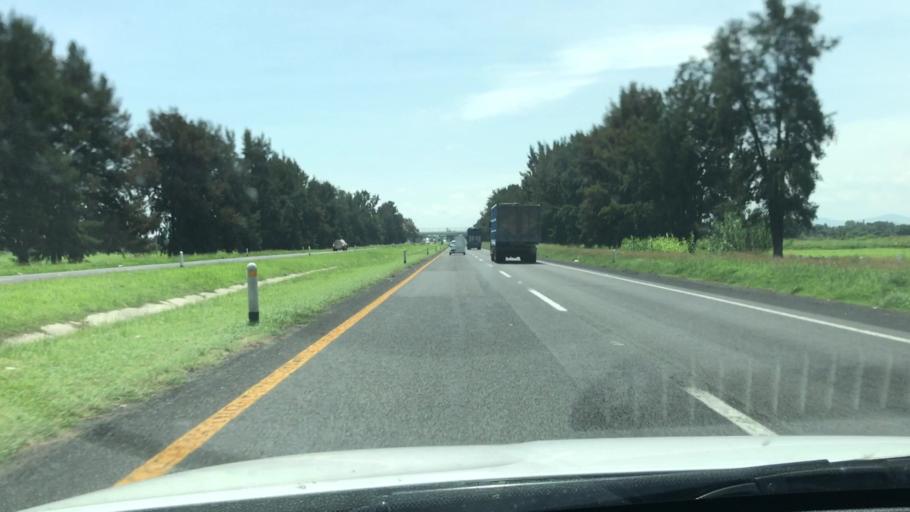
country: MX
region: Jalisco
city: La Barca
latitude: 20.3220
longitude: -102.5209
